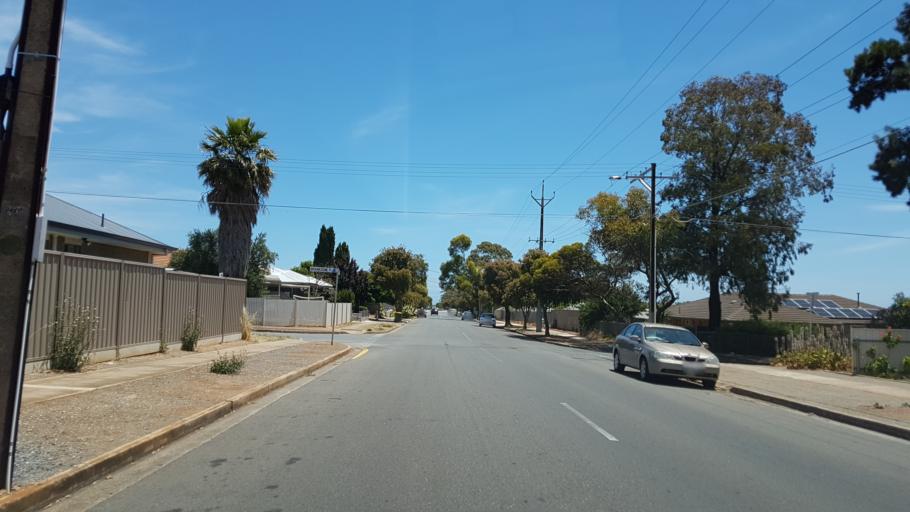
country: AU
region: South Australia
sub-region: Holdfast Bay
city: Seacliff Park
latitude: -35.0254
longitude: 138.5410
